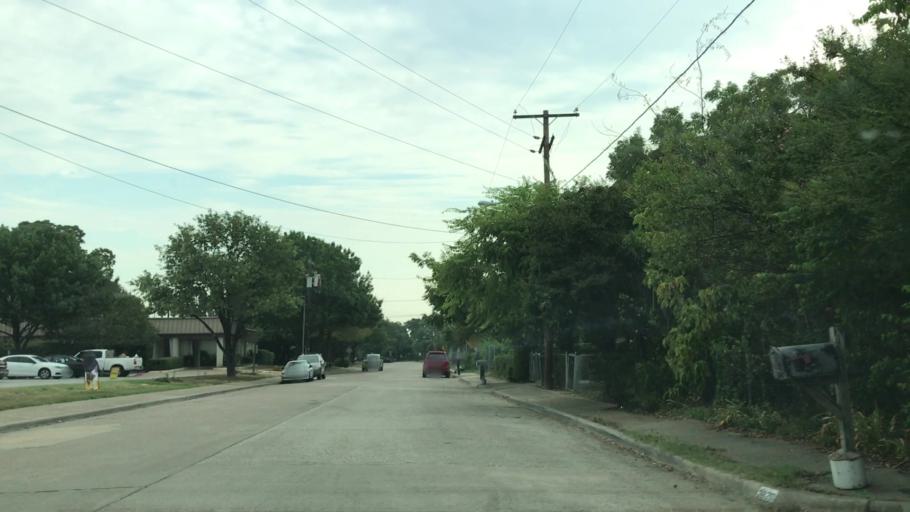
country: US
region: Texas
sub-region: Dallas County
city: Cockrell Hill
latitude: 32.7764
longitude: -96.9120
